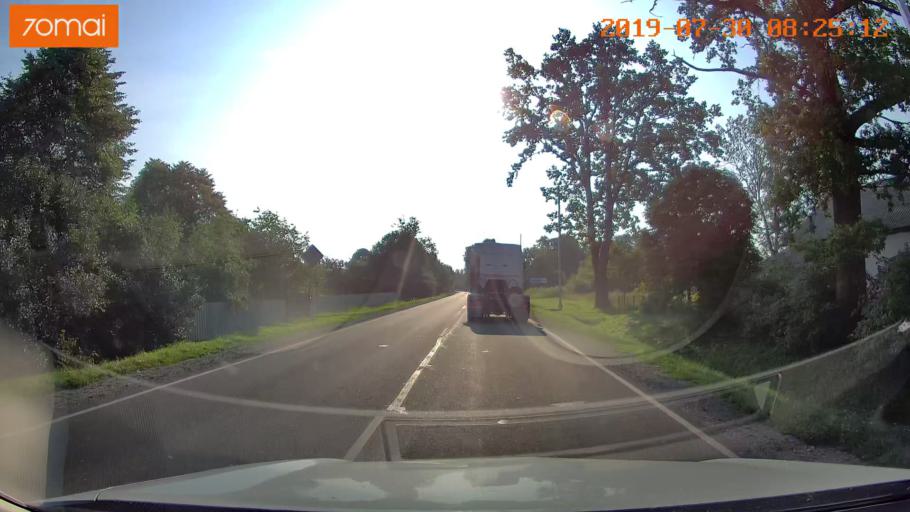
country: RU
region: Kaliningrad
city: Chernyakhovsk
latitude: 54.6238
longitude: 21.5754
